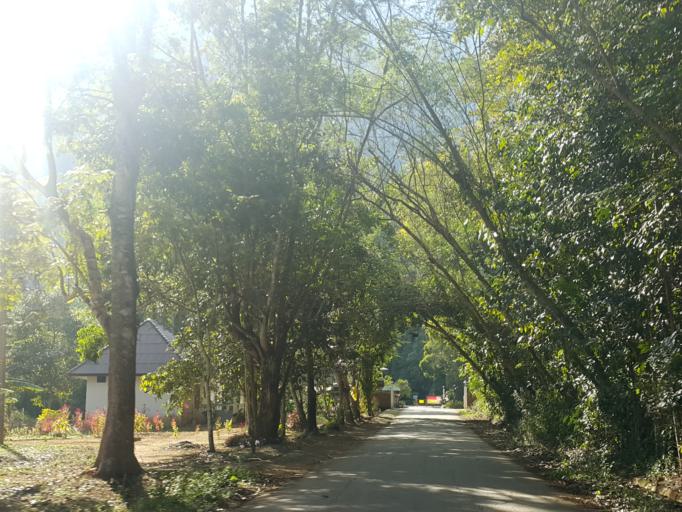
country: TH
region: Chiang Mai
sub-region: Amphoe Chiang Dao
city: Chiang Dao
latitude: 19.4019
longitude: 98.9225
